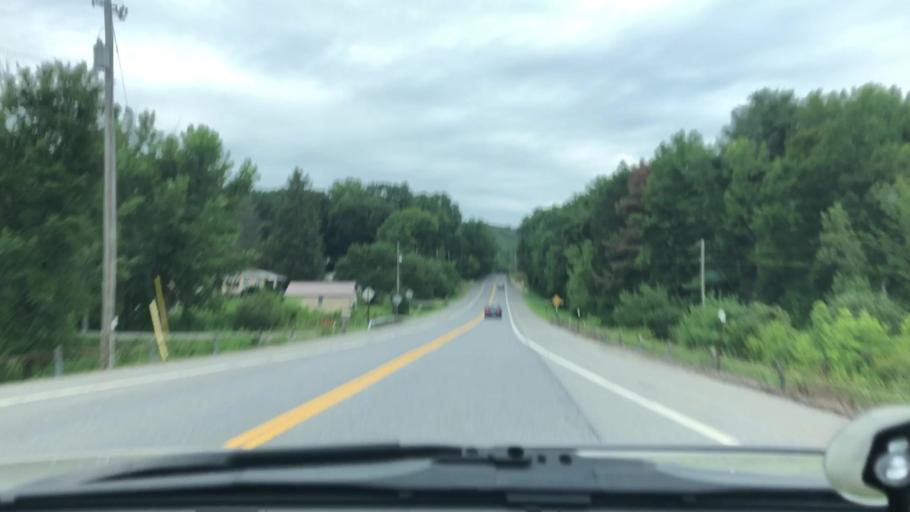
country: US
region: New York
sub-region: Saratoga County
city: Corinth
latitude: 43.1834
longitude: -73.7507
